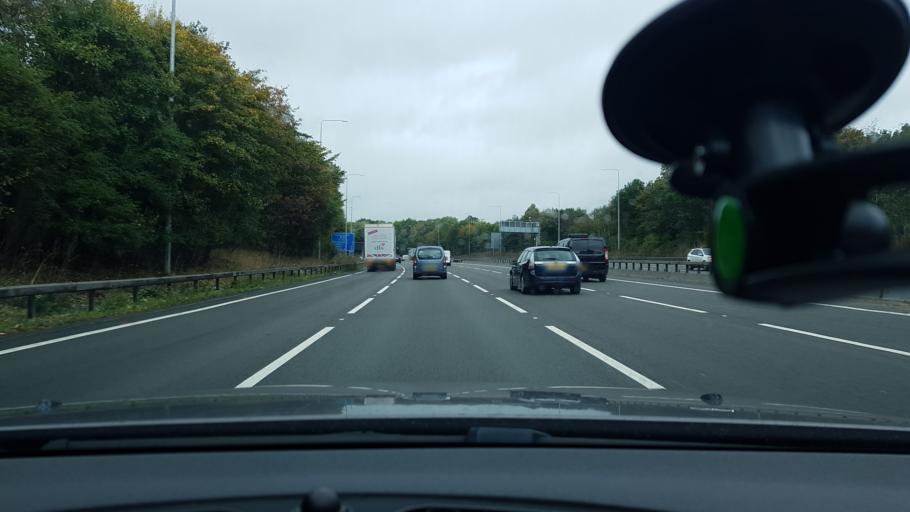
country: GB
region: England
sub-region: Essex
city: Theydon Bois
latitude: 51.6869
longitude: 0.1018
